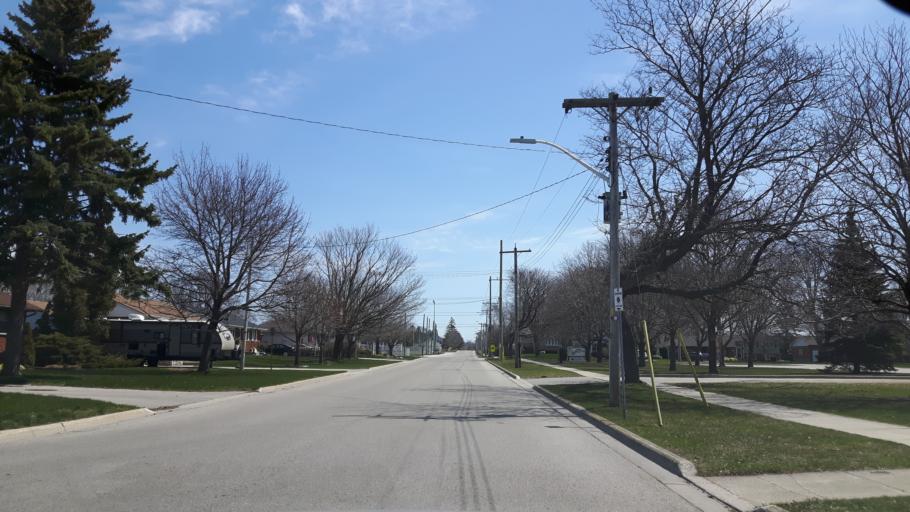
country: CA
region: Ontario
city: Goderich
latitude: 43.7355
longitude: -81.7178
